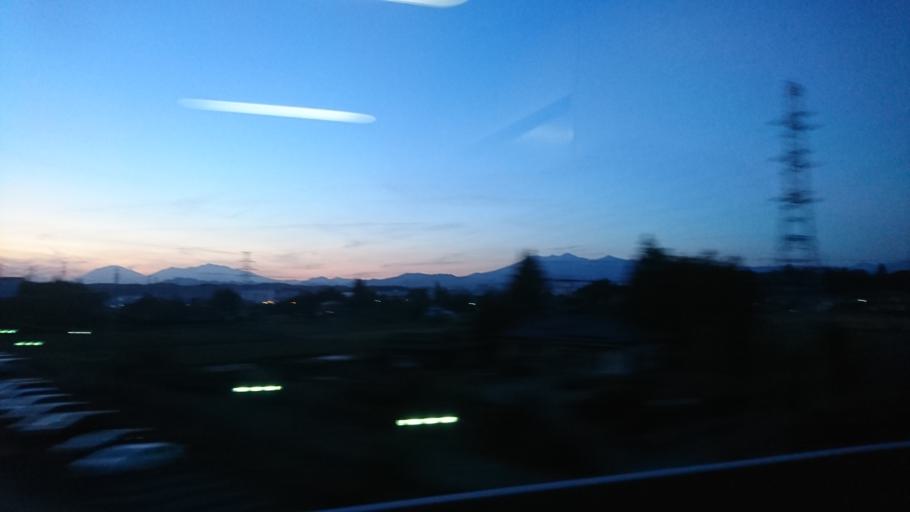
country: JP
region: Tochigi
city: Yaita
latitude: 36.7852
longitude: 139.9530
